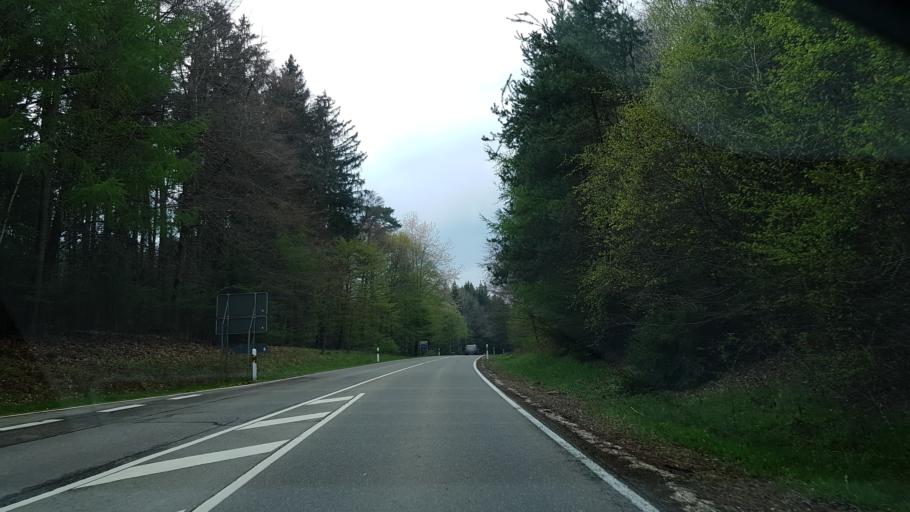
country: DE
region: Baden-Wuerttemberg
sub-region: Tuebingen Region
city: Wain
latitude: 48.2022
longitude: 10.0440
